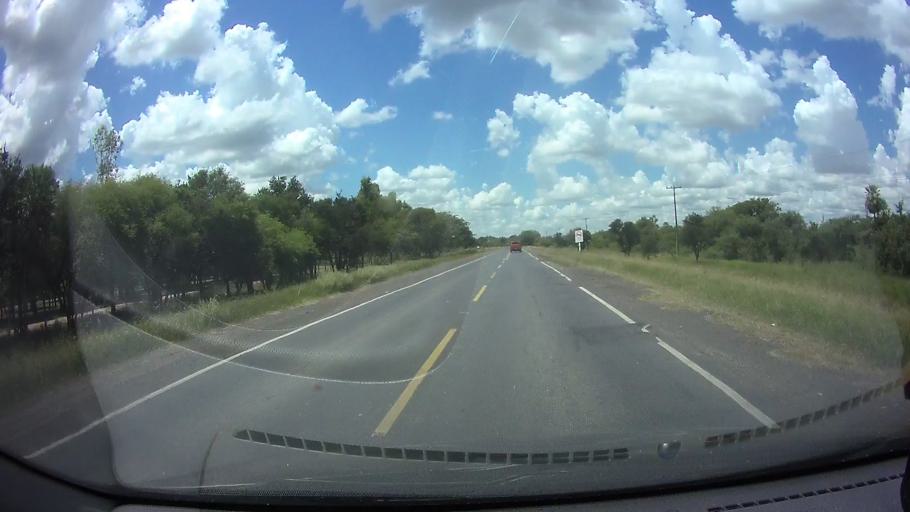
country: PY
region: Presidente Hayes
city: Nanawa
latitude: -25.2124
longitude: -57.6614
